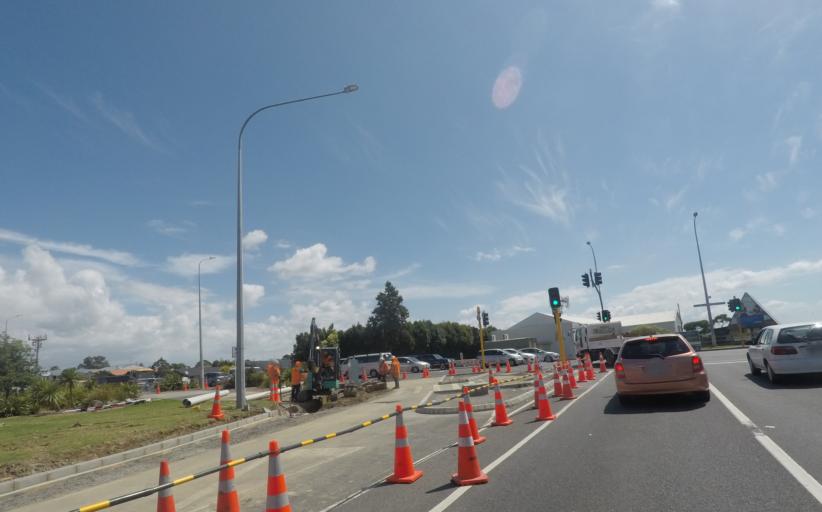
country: NZ
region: Auckland
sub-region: Auckland
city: Tamaki
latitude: -36.8683
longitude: 174.8457
